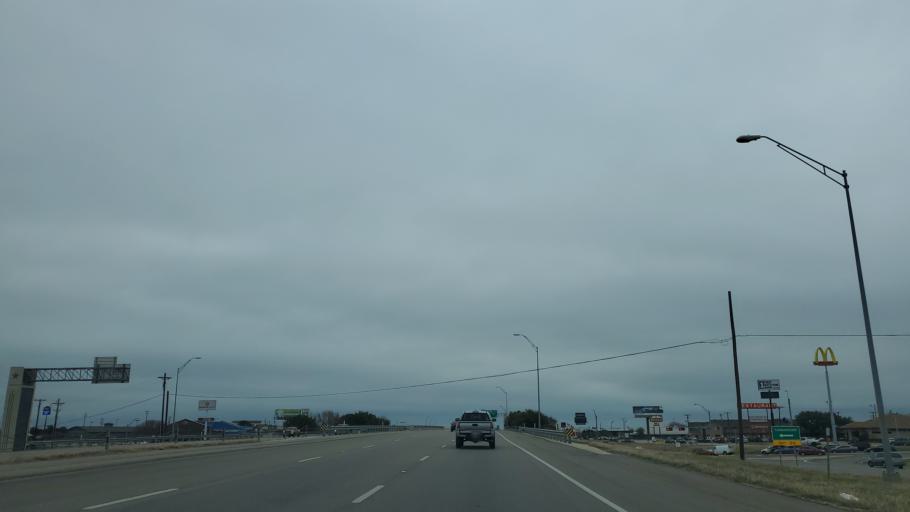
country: US
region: Texas
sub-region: Bell County
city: Harker Heights
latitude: 31.0811
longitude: -97.7003
